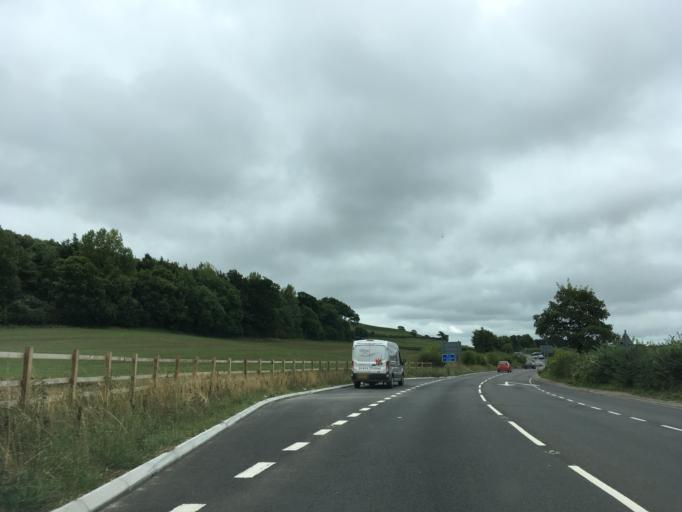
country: GB
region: England
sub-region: Bath and North East Somerset
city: Saltford
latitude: 51.3729
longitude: -2.4777
